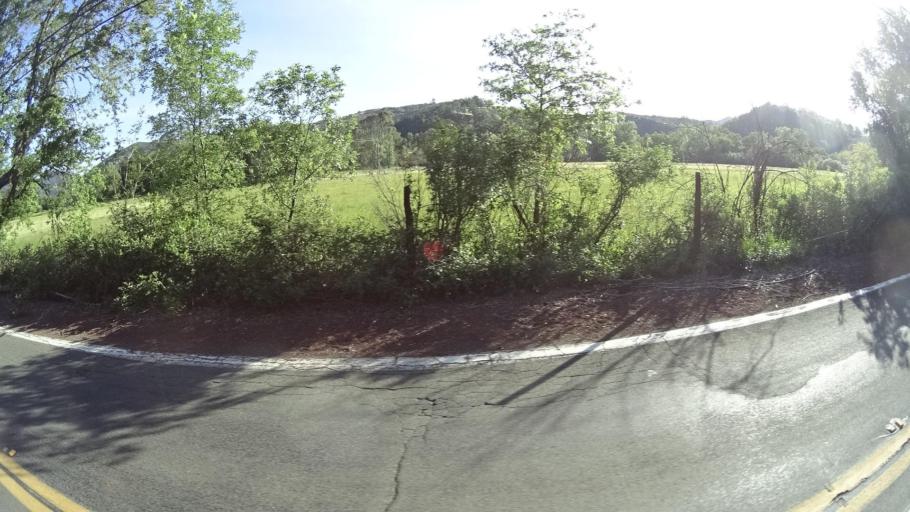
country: US
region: California
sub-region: Lake County
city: North Lakeport
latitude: 39.1150
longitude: -122.9856
